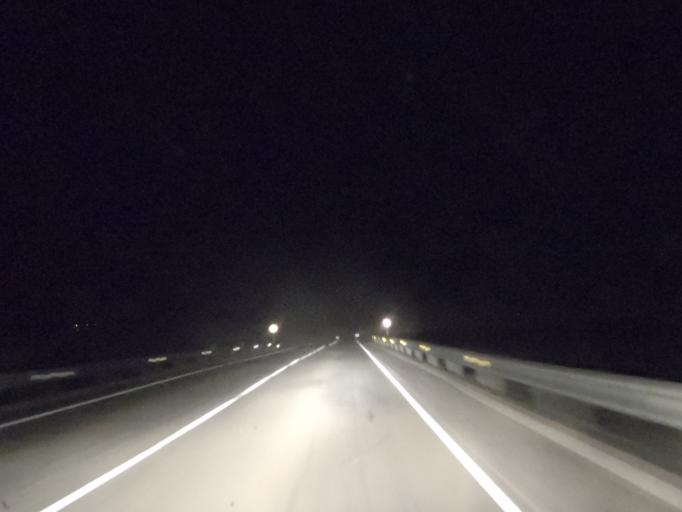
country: ES
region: Castille and Leon
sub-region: Provincia de Zamora
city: Santa Cristina de la Polvorosa
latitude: 42.0246
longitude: -5.7010
